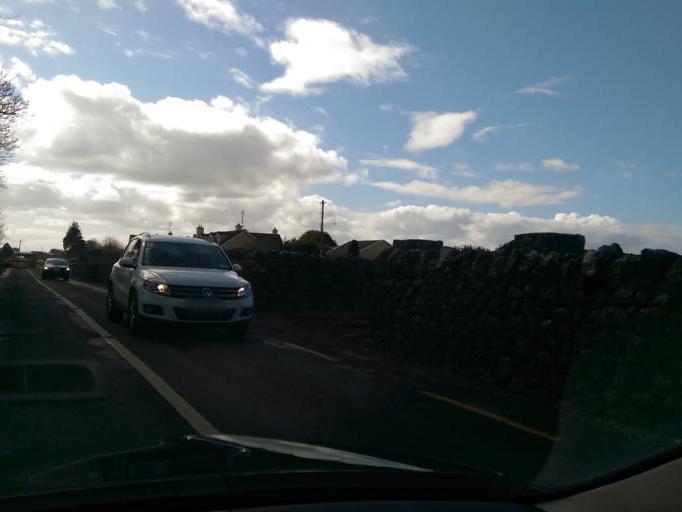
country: IE
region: Connaught
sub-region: County Galway
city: Athenry
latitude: 53.3700
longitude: -8.7118
